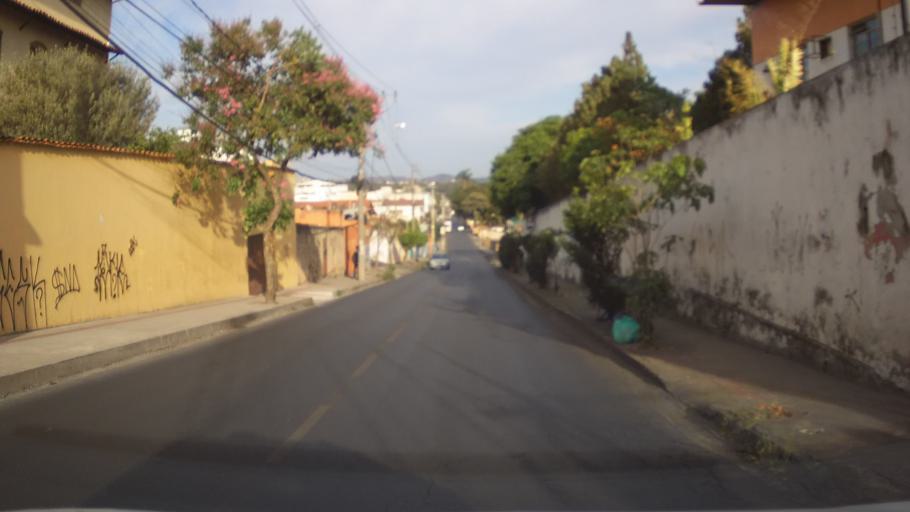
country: BR
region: Minas Gerais
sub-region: Belo Horizonte
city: Belo Horizonte
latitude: -19.8712
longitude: -43.9904
